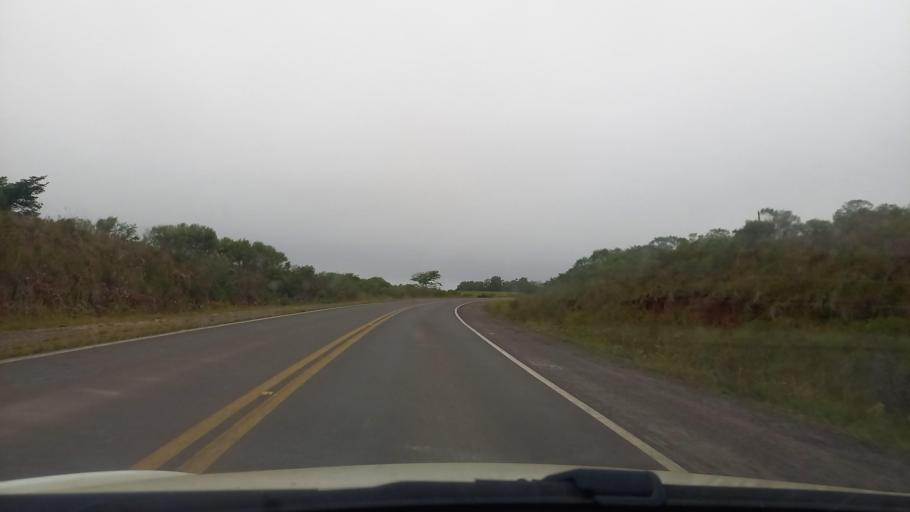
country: BR
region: Rio Grande do Sul
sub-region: Rosario Do Sul
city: Rosario do Sul
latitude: -30.1661
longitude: -54.6841
